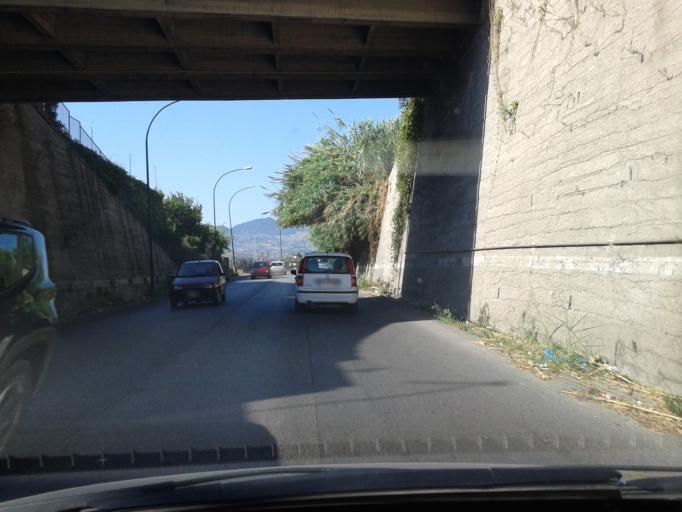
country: IT
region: Sicily
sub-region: Palermo
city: Monreale
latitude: 38.0752
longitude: 13.2873
